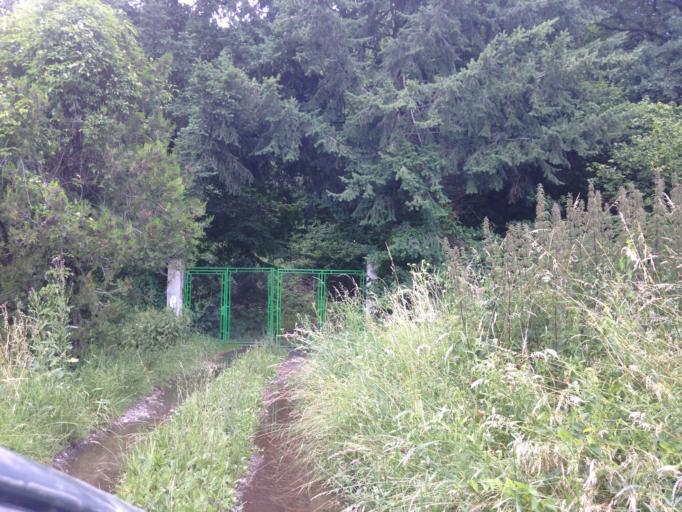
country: RO
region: Cluj
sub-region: Comuna Feleacu
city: Feleacu
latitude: 46.7247
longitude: 23.5819
